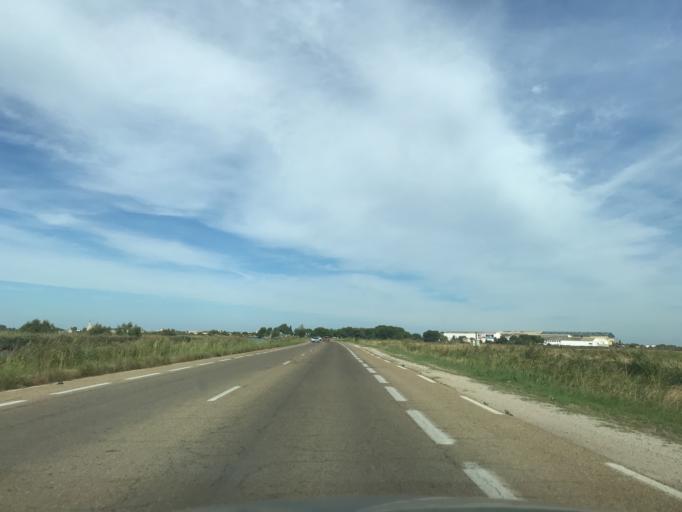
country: FR
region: Languedoc-Roussillon
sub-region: Departement du Gard
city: Aigues-Mortes
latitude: 43.5533
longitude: 4.1738
